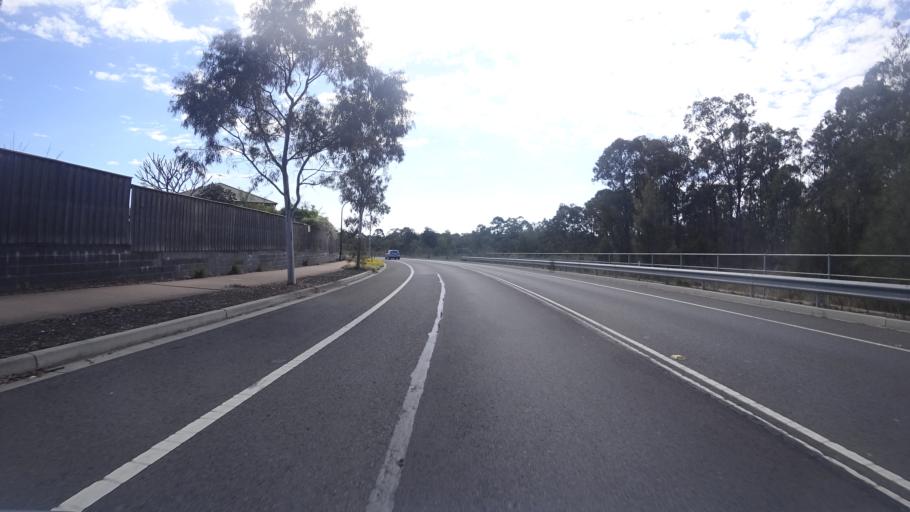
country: AU
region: New South Wales
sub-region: Bankstown
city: Milperra
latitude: -33.9412
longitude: 150.9582
